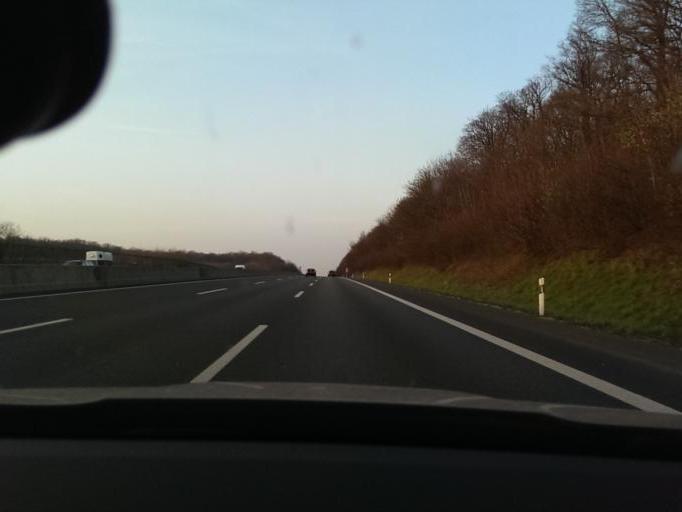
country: DE
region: Lower Saxony
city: Hillerse
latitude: 51.6671
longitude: 9.9197
